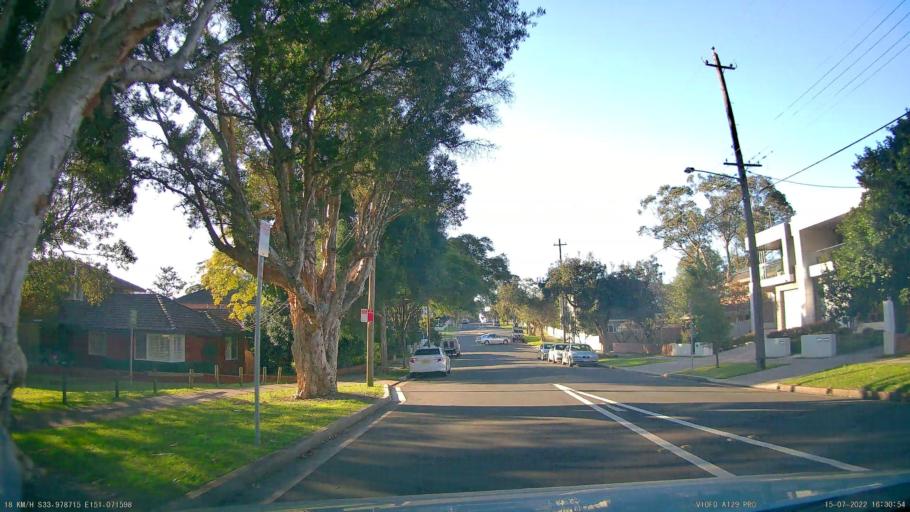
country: AU
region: New South Wales
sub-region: Hurstville
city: Oatley
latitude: -33.9786
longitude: 151.0716
